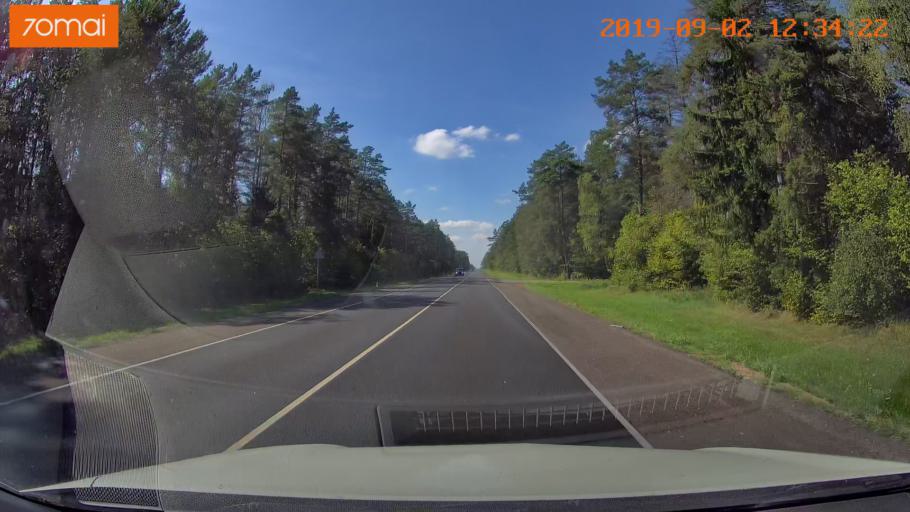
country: RU
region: Smolensk
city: Shumyachi
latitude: 53.8109
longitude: 32.4063
